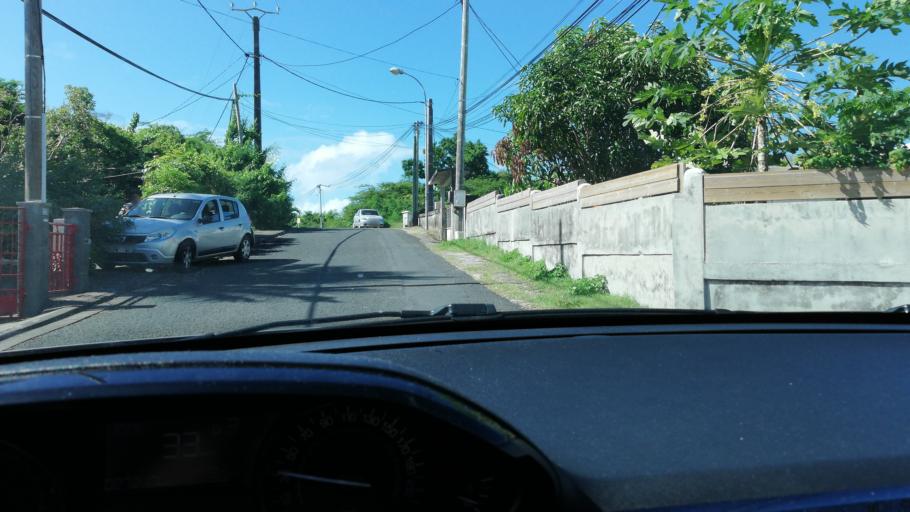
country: GP
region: Guadeloupe
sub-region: Guadeloupe
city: Le Gosier
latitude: 16.2128
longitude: -61.4554
